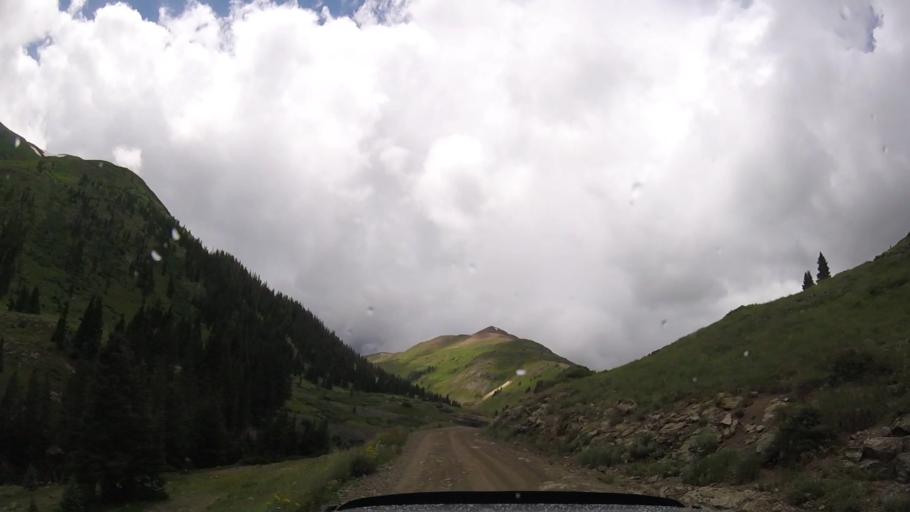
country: US
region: Colorado
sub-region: Ouray County
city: Ouray
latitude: 37.9287
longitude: -107.5658
